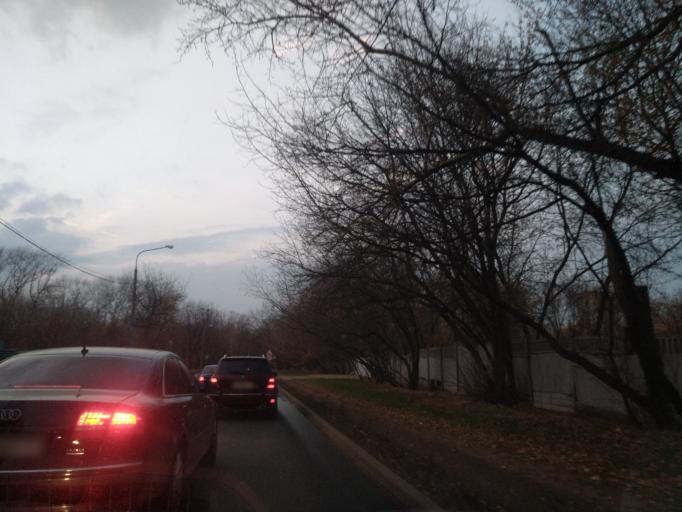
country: RU
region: Moscow
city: Leonovo
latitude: 55.8635
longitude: 37.6443
